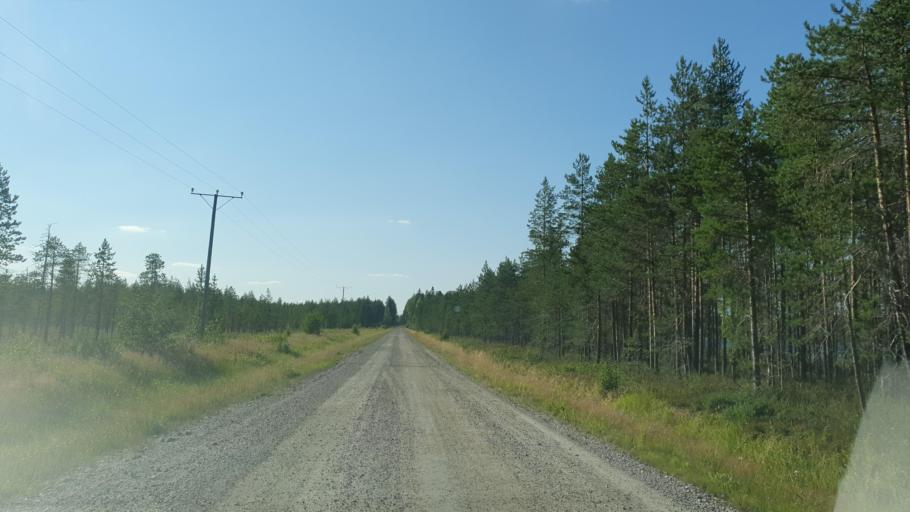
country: FI
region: Kainuu
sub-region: Kehys-Kainuu
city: Kuhmo
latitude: 64.0209
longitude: 29.7349
